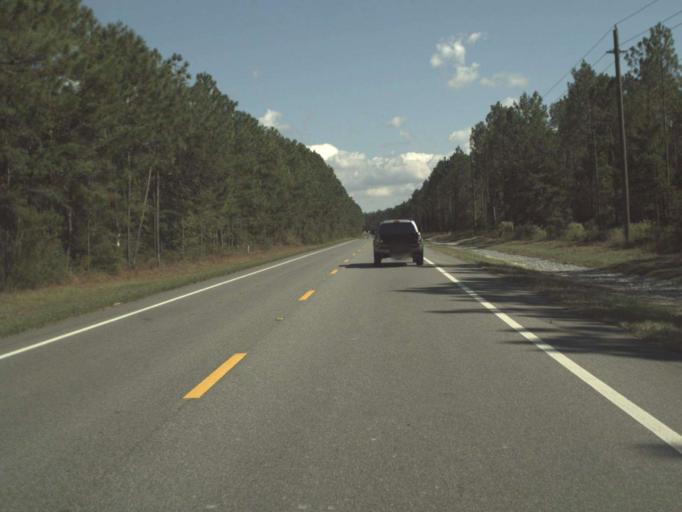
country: US
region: Florida
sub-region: Walton County
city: Freeport
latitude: 30.4847
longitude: -86.1075
